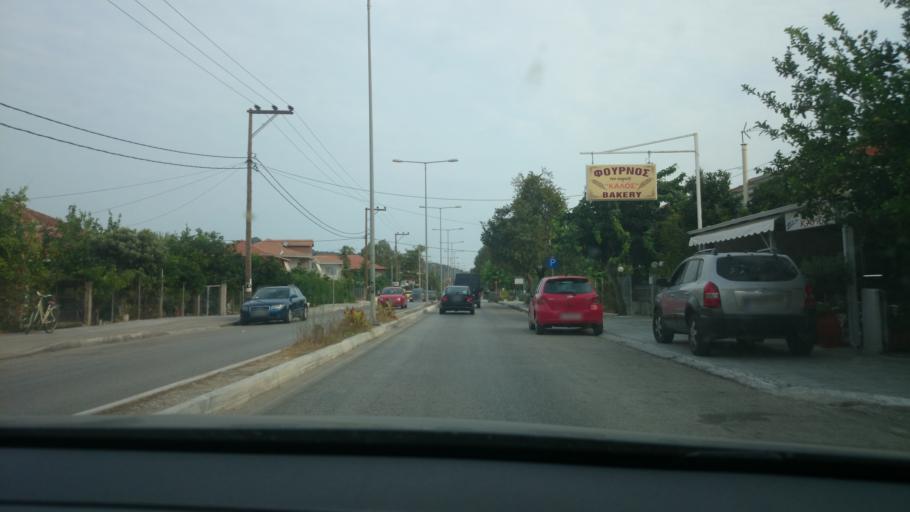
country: GR
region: Ionian Islands
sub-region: Lefkada
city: Lefkada
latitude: 38.7942
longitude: 20.7177
